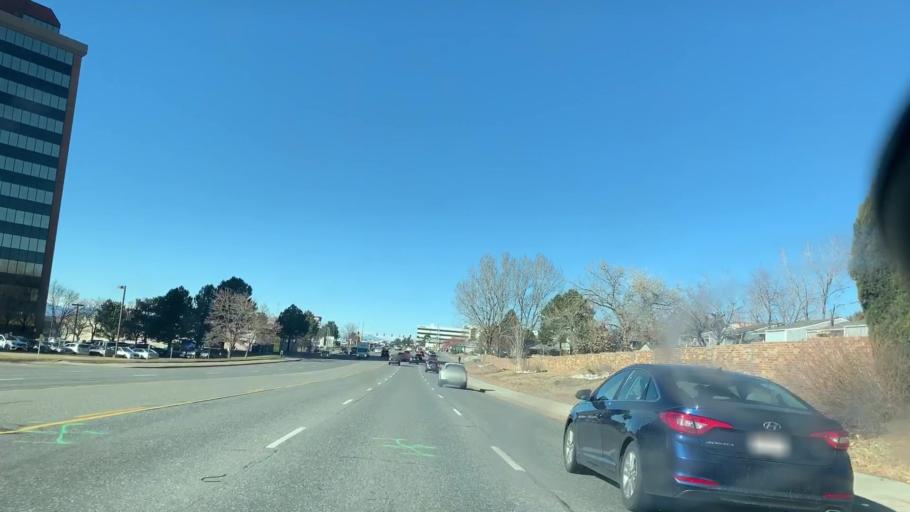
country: US
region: Colorado
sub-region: Adams County
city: Aurora
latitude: 39.6649
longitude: -104.8596
